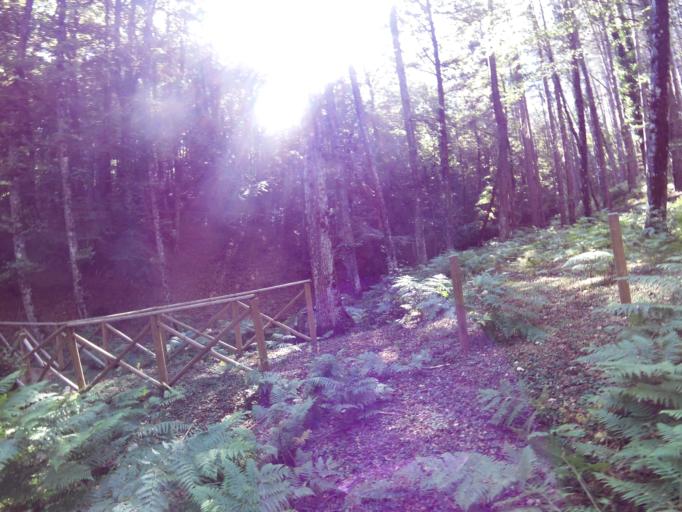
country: IT
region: Calabria
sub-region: Provincia di Vibo-Valentia
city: Nardodipace
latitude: 38.5038
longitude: 16.3748
